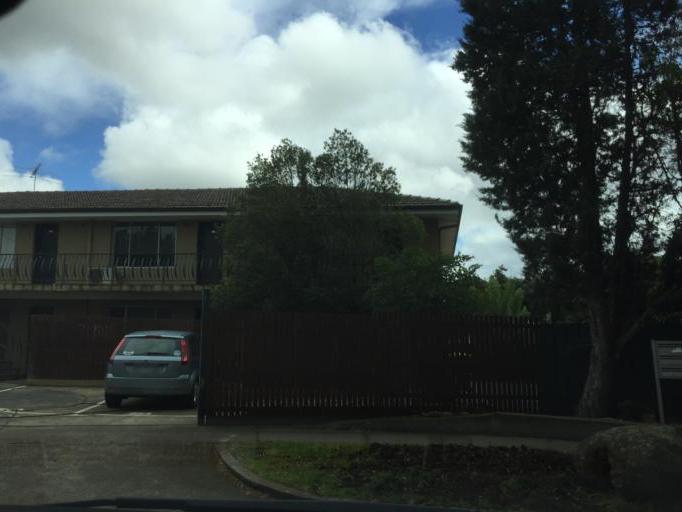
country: AU
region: Victoria
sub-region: Brimbank
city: Sunshine North
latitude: -37.7802
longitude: 144.8251
